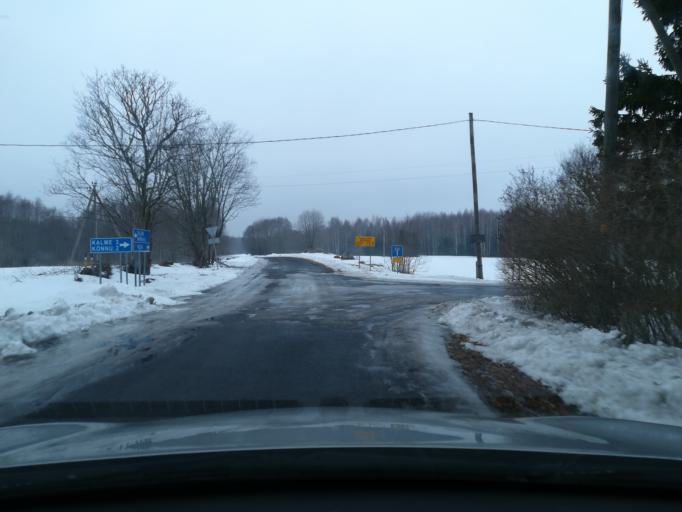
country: EE
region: Harju
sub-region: Loksa linn
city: Loksa
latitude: 59.4652
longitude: 25.7041
